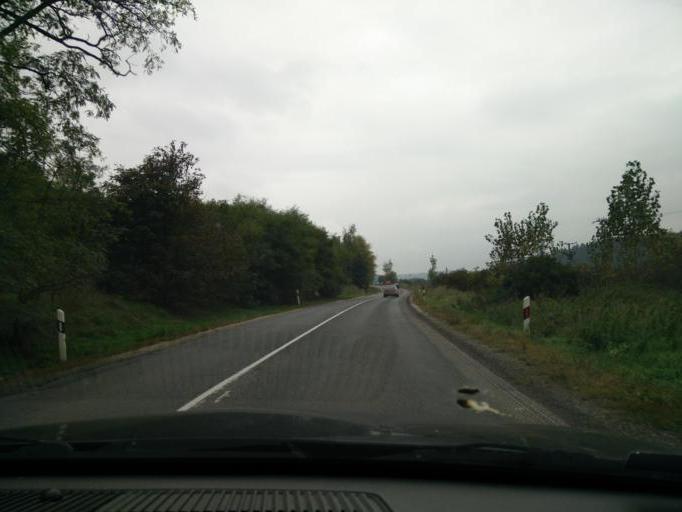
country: HU
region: Komarom-Esztergom
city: Piliscsev
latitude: 47.6661
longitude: 18.7812
